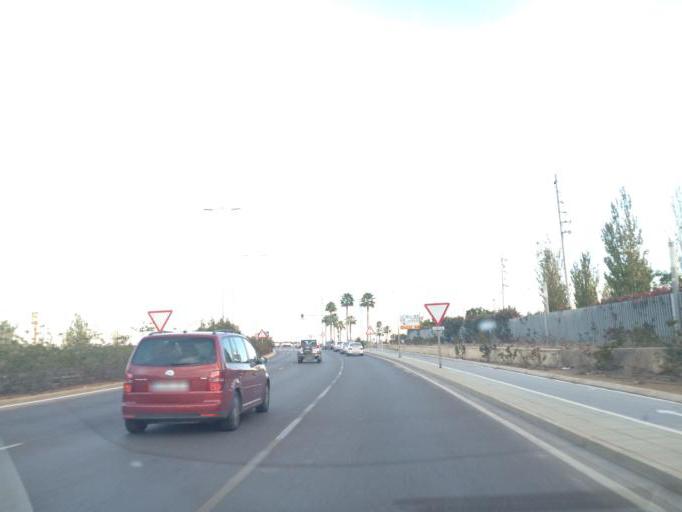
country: ES
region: Andalusia
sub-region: Provincia de Almeria
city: Almeria
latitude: 36.8417
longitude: -2.4350
